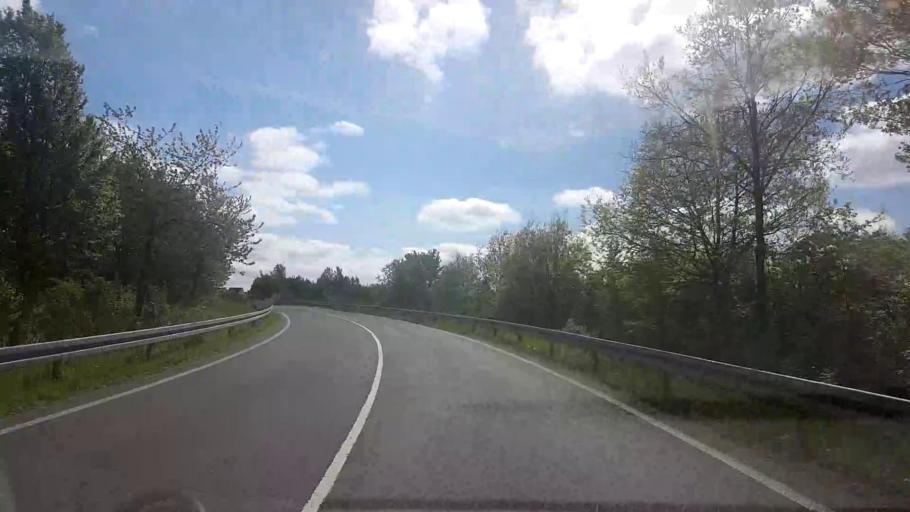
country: DE
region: Bavaria
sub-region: Upper Franconia
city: Untersiemau
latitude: 50.2037
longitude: 10.9683
